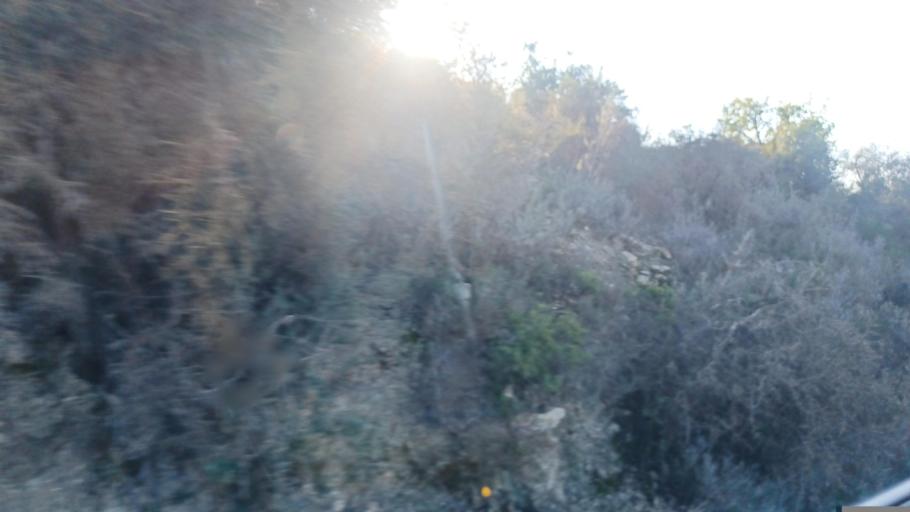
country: CY
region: Larnaka
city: Kofinou
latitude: 34.8422
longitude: 33.3036
